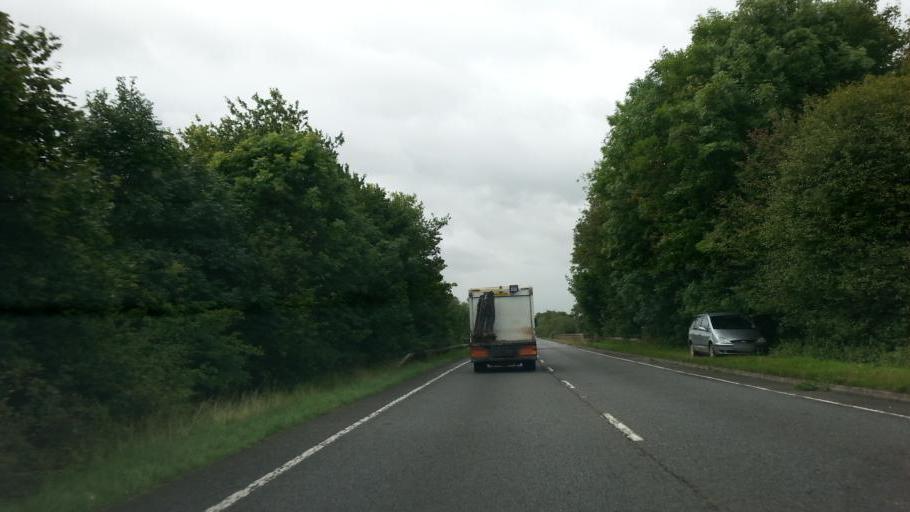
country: GB
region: England
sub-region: Northamptonshire
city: Oundle
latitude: 52.4719
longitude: -0.4574
